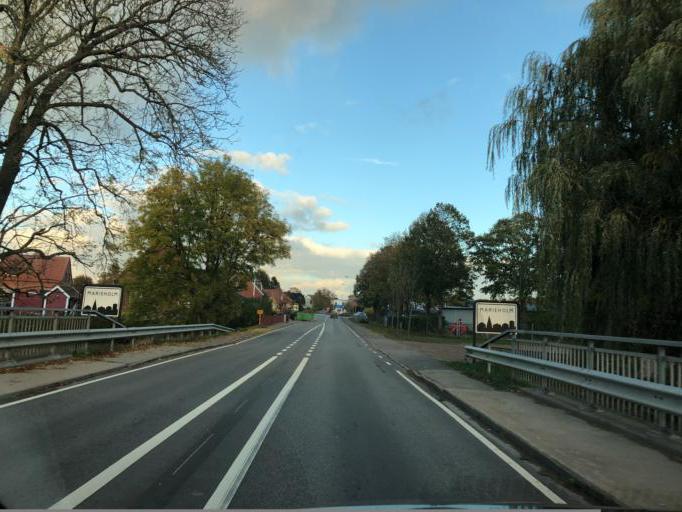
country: SE
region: Skane
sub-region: Svalovs Kommun
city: Teckomatorp
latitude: 55.8621
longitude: 13.1427
